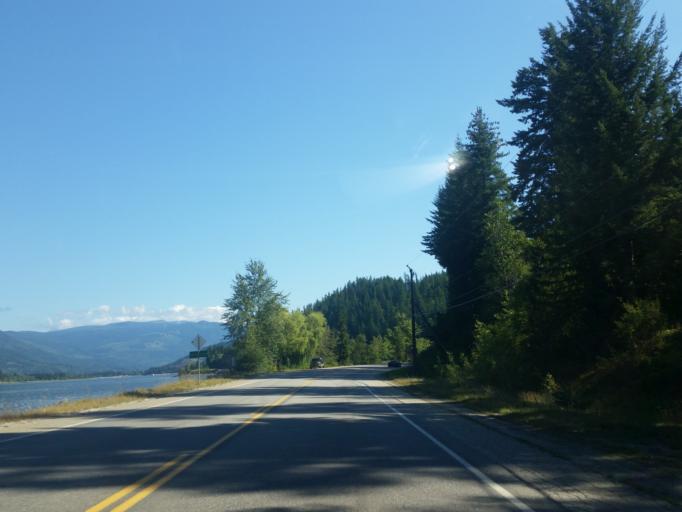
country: CA
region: British Columbia
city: Sicamous
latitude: 50.7796
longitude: -119.0009
